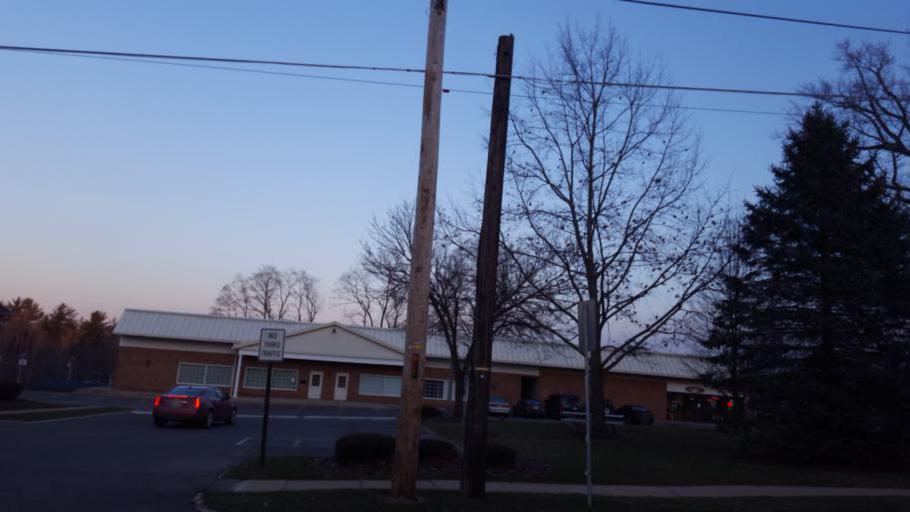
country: US
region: Ohio
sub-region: Richland County
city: Lexington
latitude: 40.6791
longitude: -82.5828
